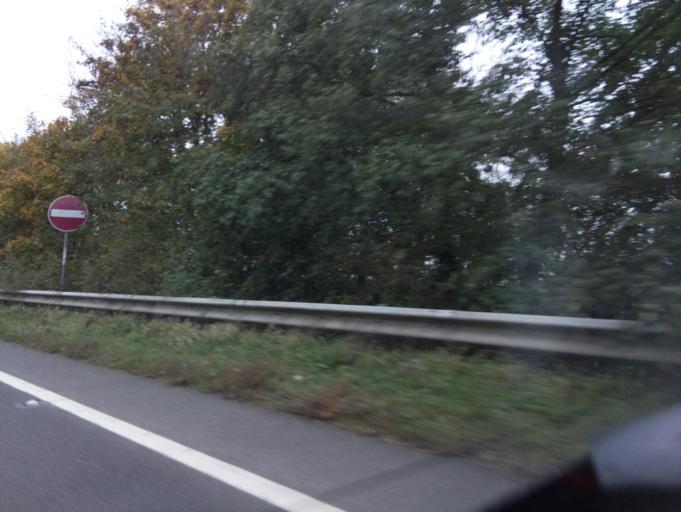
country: GB
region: England
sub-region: Somerset
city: Stoke-sub-Hamdon
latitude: 50.9563
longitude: -2.7630
